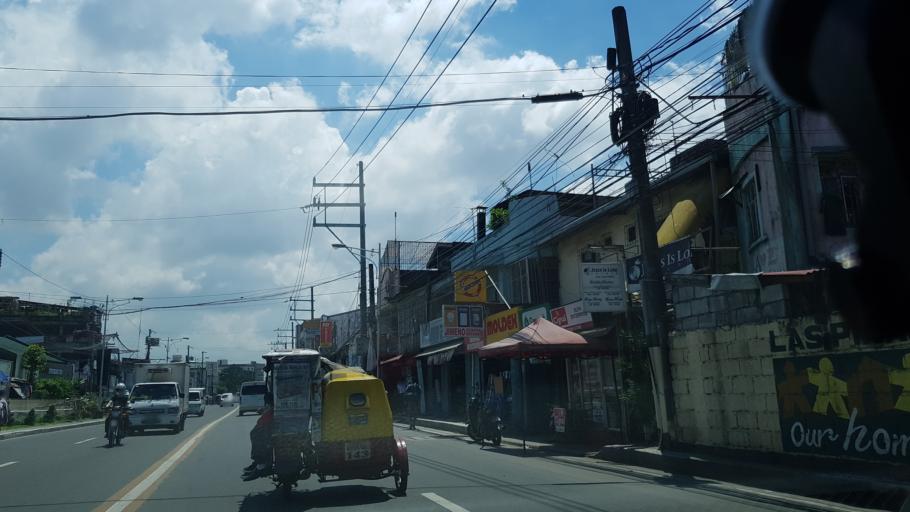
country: PH
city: Sambayanihan People's Village
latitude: 14.4591
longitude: 120.9947
